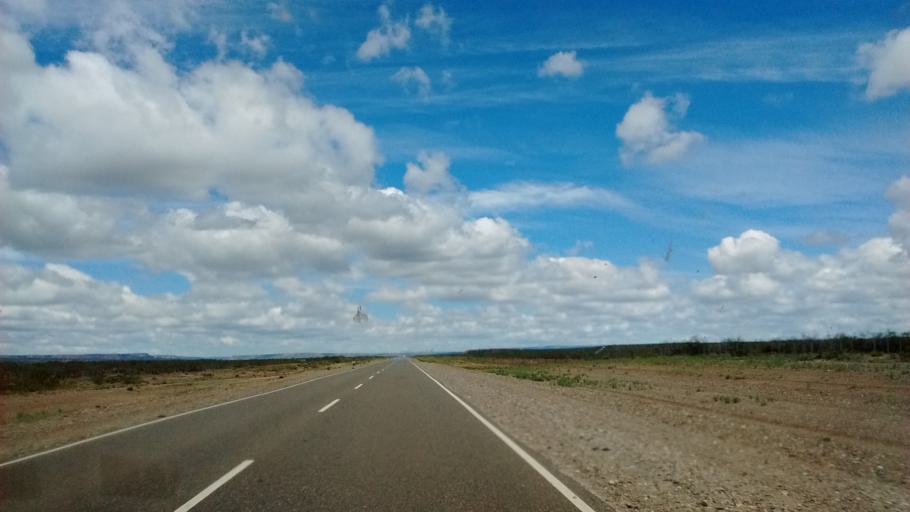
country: AR
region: Neuquen
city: Piedra del Aguila
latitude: -39.8307
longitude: -69.7564
